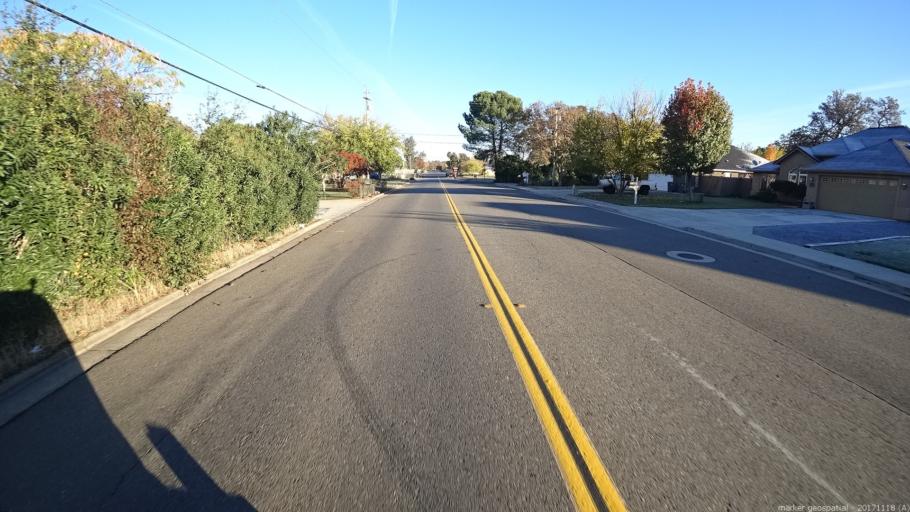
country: US
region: California
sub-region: Shasta County
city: Cottonwood
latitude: 40.3968
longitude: -122.2891
